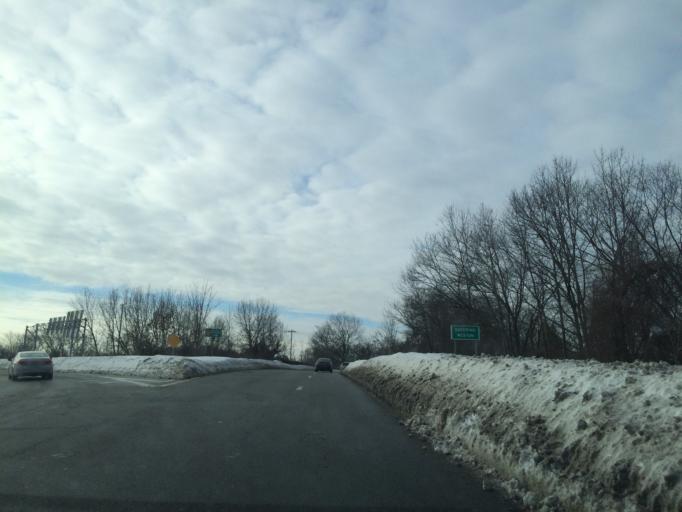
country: US
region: Massachusetts
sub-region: Middlesex County
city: Weston
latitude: 42.3706
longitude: -71.2712
